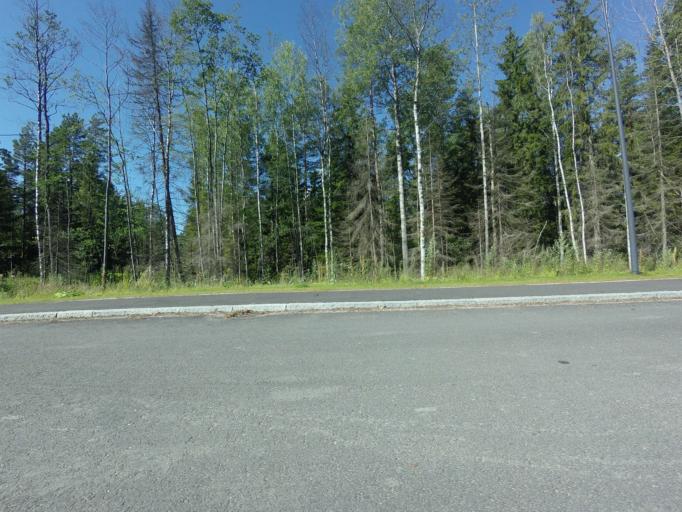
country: FI
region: Uusimaa
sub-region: Helsinki
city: Espoo
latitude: 60.1501
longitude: 24.5952
